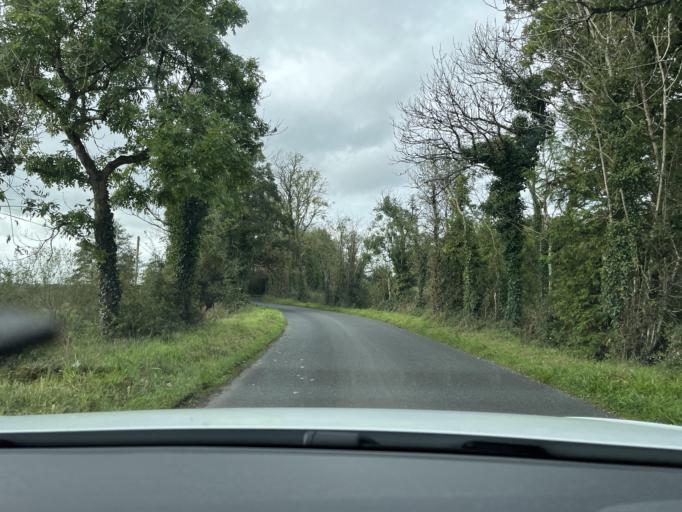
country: IE
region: Connaught
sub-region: County Leitrim
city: Carrick-on-Shannon
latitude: 53.9665
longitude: -8.0897
